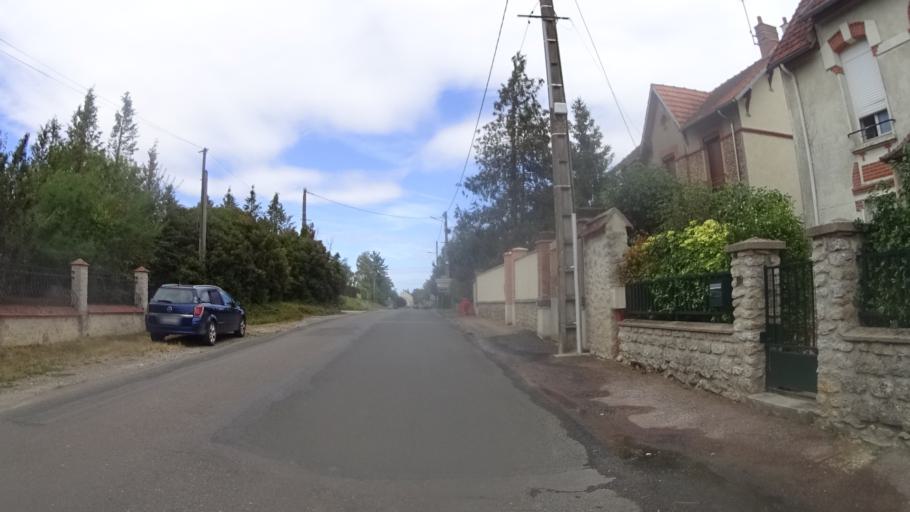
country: FR
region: Centre
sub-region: Departement du Loiret
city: Malesherbes
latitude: 48.2309
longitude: 2.4282
